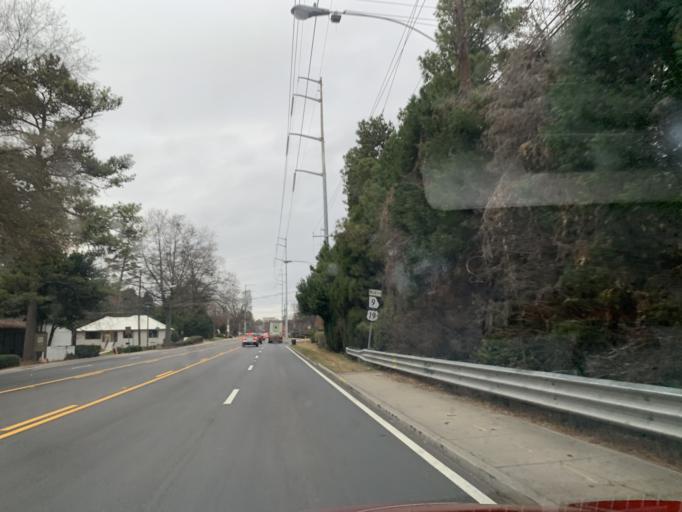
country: US
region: Georgia
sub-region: Fulton County
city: Sandy Springs
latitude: 33.8943
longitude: -84.3813
